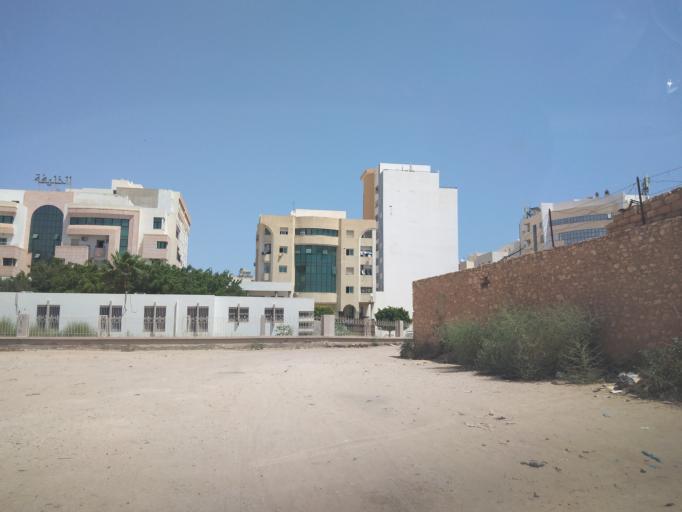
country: TN
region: Safaqis
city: Sfax
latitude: 34.7360
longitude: 10.7506
